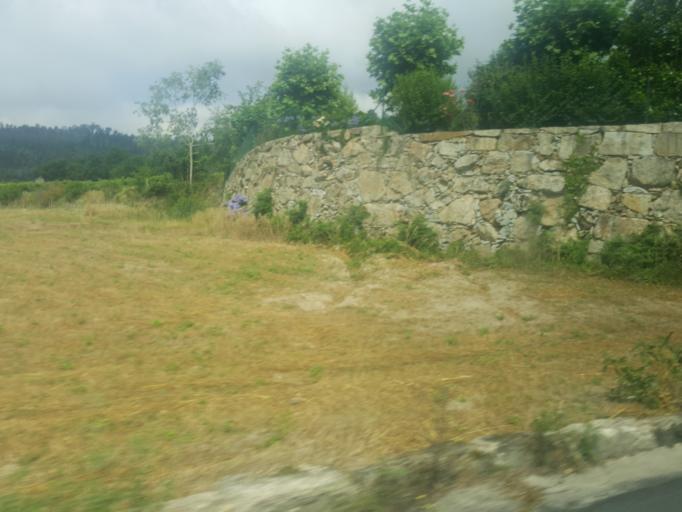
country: PT
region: Porto
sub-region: Marco de Canaveses
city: Marco de Canavezes
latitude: 41.1783
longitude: -8.1935
